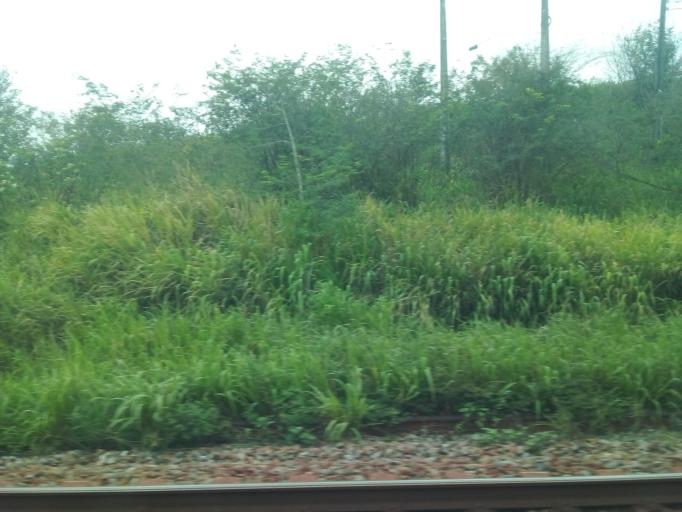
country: BR
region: Maranhao
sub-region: Santa Ines
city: Santa Ines
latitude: -3.6843
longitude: -45.3440
